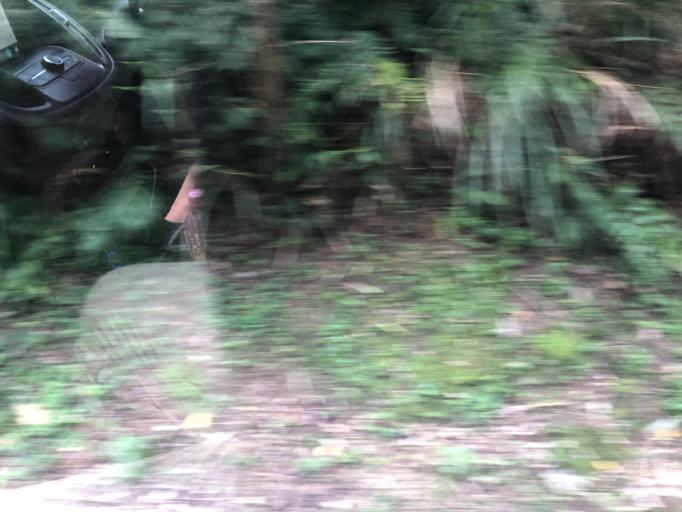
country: TW
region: Taiwan
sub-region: Taoyuan
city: Taoyuan
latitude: 24.9115
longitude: 121.4074
